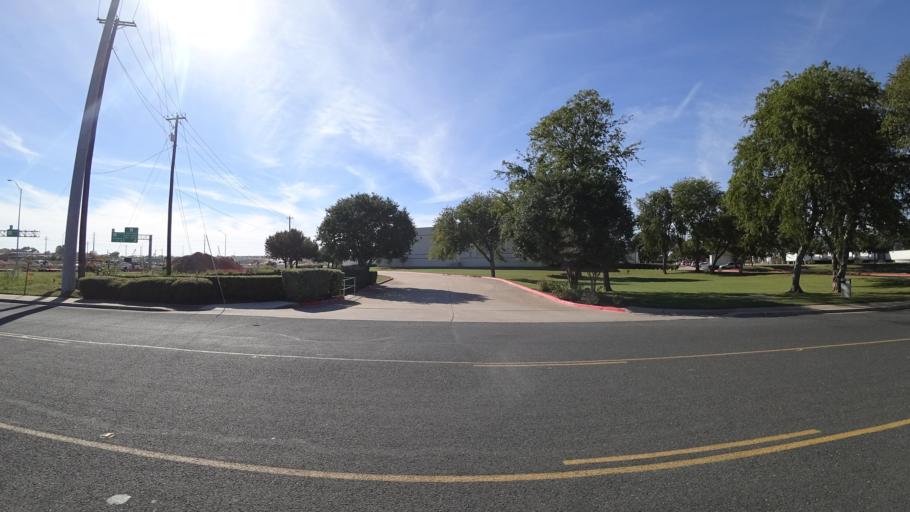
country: US
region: Texas
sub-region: Travis County
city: Austin
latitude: 30.2515
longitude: -97.6849
